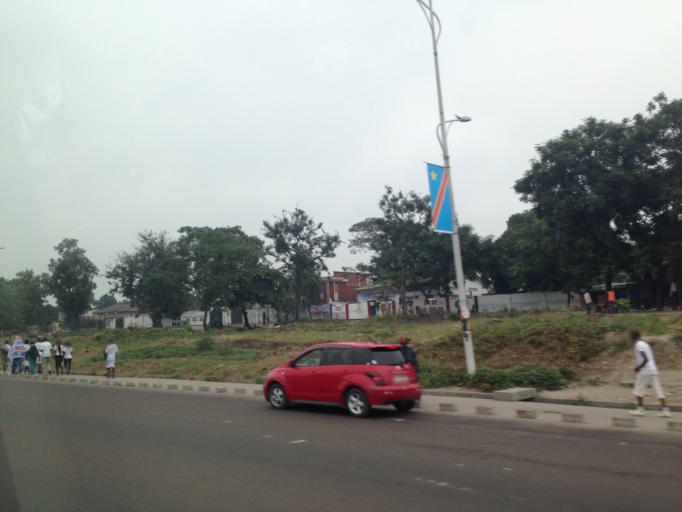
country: CD
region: Kinshasa
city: Kinshasa
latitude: -4.3455
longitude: 15.3313
